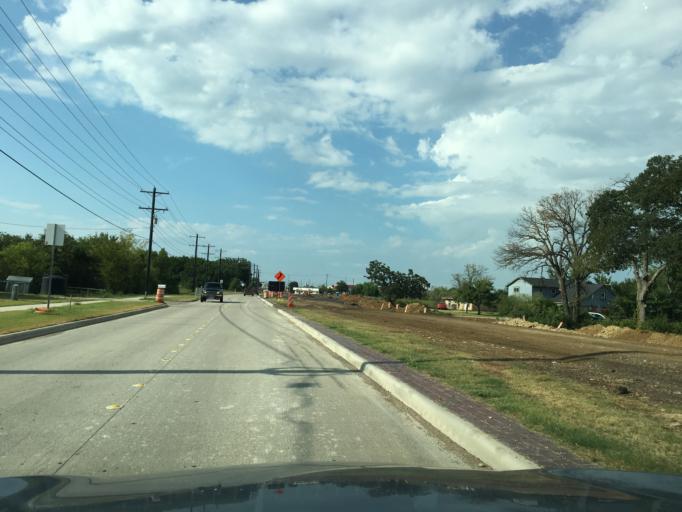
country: US
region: Texas
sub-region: Denton County
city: Denton
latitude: 33.2305
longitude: -97.0829
